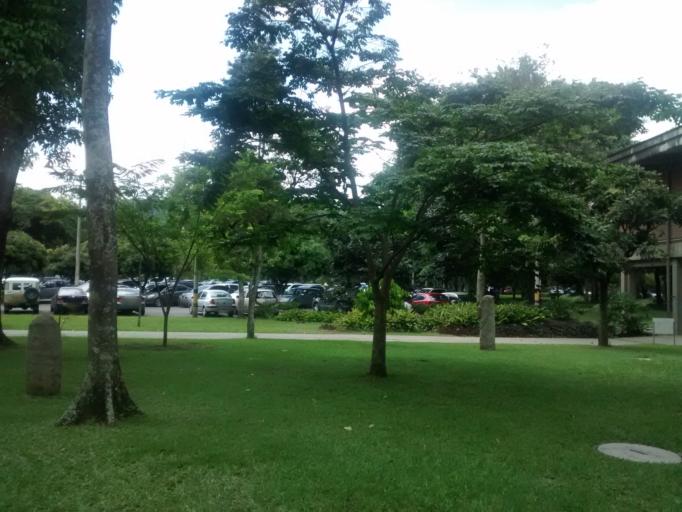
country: CO
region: Antioquia
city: Medellin
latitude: 6.2676
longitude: -75.5699
